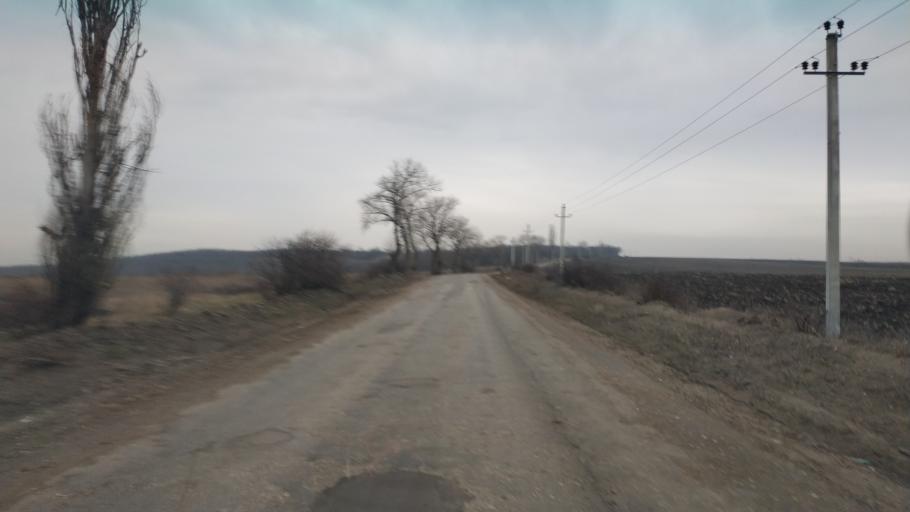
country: MD
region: Chisinau
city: Singera
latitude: 46.8512
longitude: 29.0029
